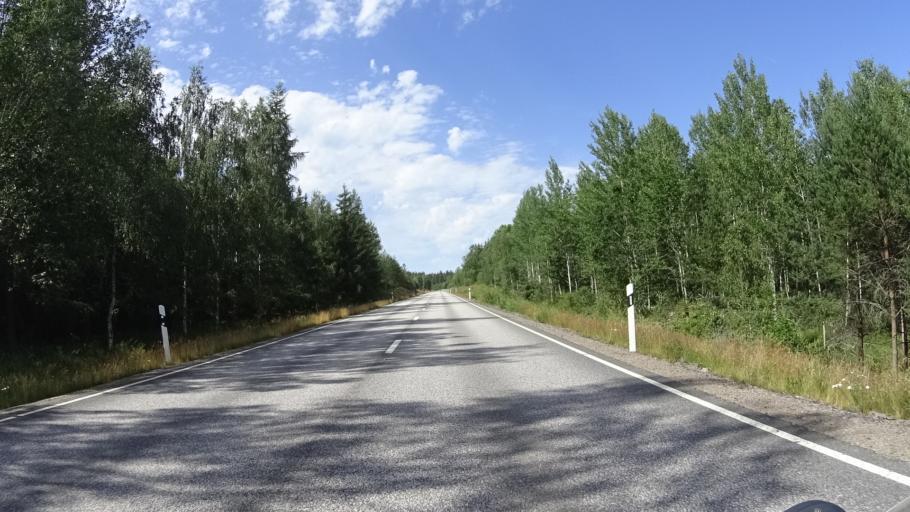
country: SE
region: Kalmar
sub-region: Vasterviks Kommun
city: Overum
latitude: 58.0644
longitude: 16.2030
